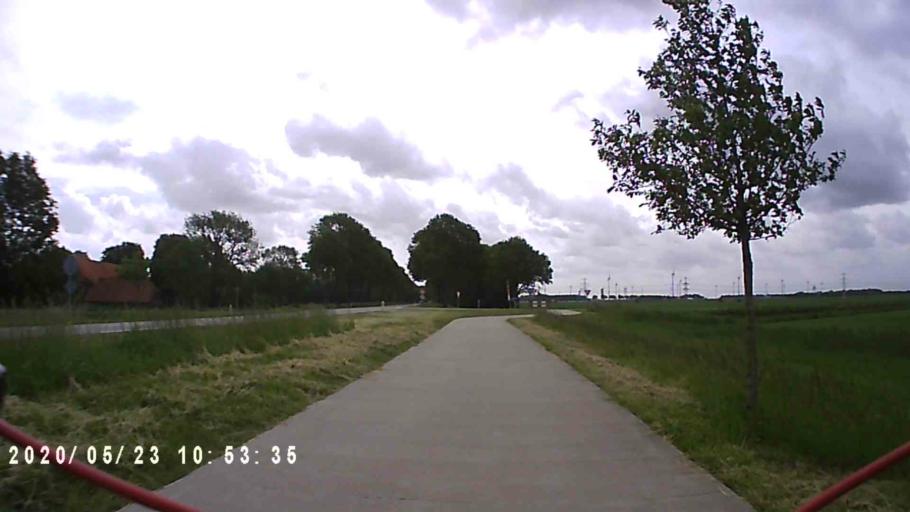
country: NL
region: Groningen
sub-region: Gemeente Delfzijl
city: Delfzijl
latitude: 53.3105
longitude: 6.9439
